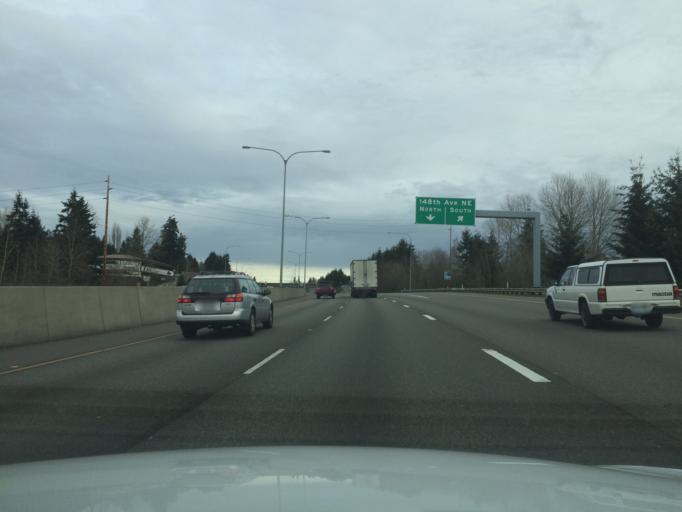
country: US
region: Washington
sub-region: King County
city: Redmond
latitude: 47.6305
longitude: -122.1501
